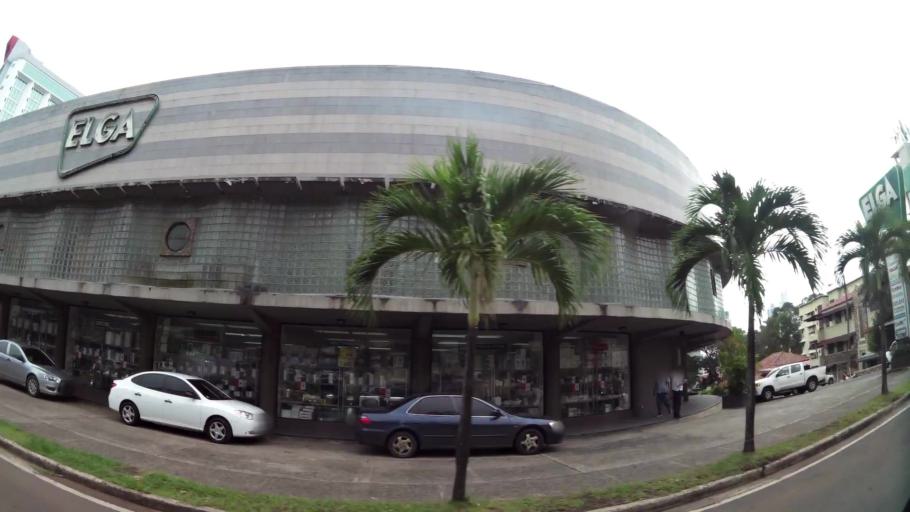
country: PA
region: Panama
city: Panama
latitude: 8.9793
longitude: -79.5299
